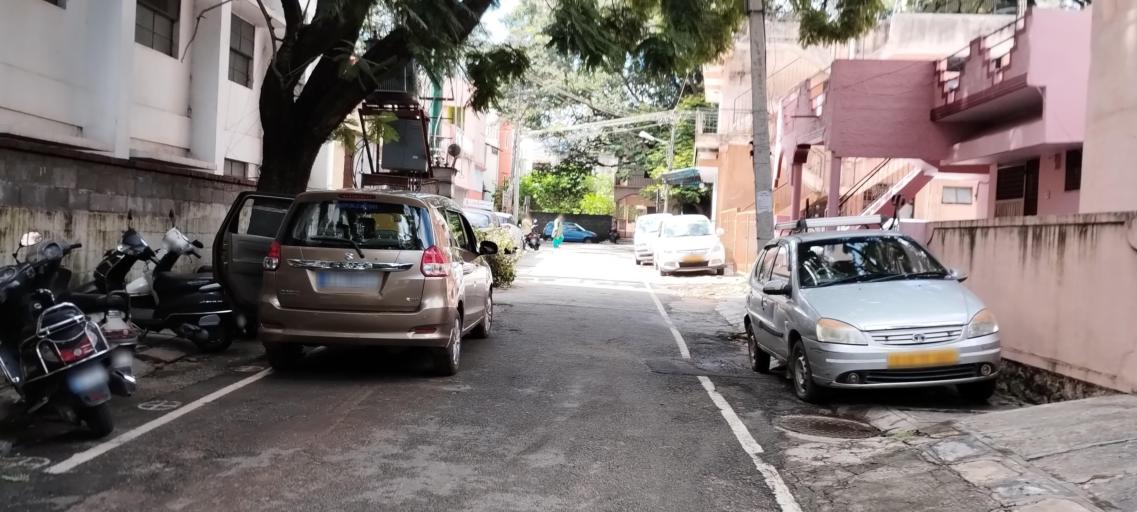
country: IN
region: Karnataka
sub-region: Bangalore Urban
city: Bangalore
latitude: 12.9414
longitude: 77.5403
